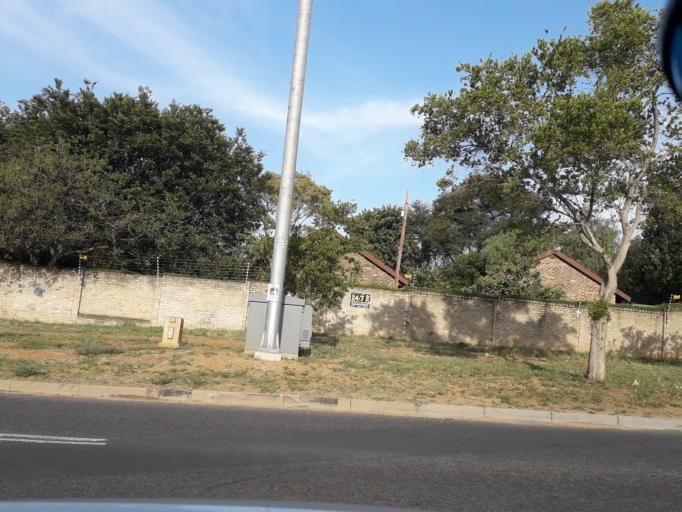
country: ZA
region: Gauteng
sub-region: City of Johannesburg Metropolitan Municipality
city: Diepsloot
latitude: -26.0299
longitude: 27.9918
